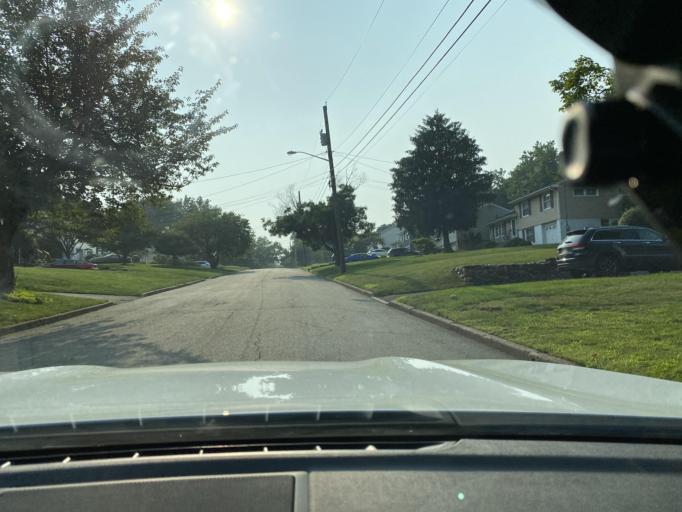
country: US
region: New York
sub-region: Rockland County
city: Airmont
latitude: 41.0930
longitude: -74.1282
